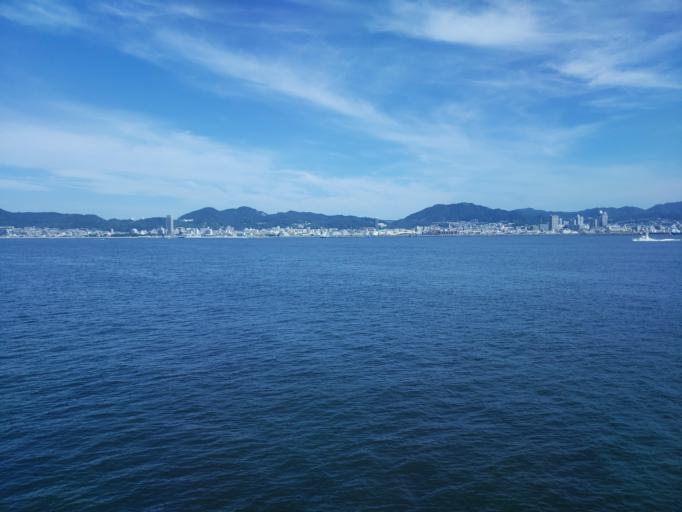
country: JP
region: Hyogo
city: Kobe
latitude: 34.6267
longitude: 135.1510
